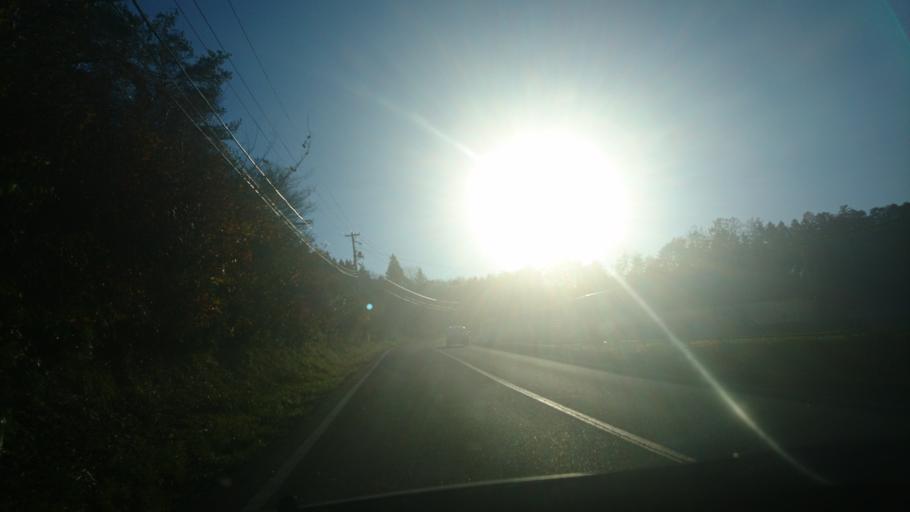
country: JP
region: Iwate
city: Ichinoseki
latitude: 38.9025
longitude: 141.2178
